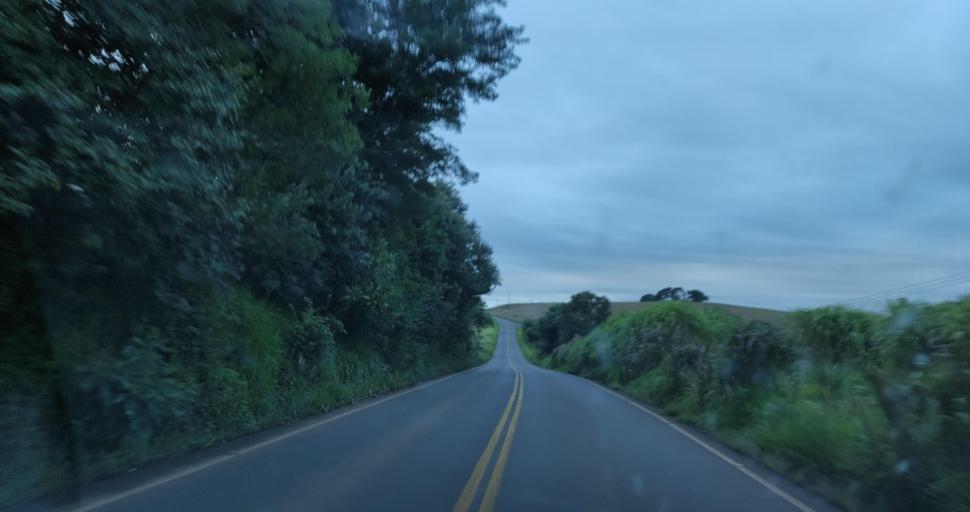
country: BR
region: Santa Catarina
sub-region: Xanxere
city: Xanxere
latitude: -26.7261
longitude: -52.4068
